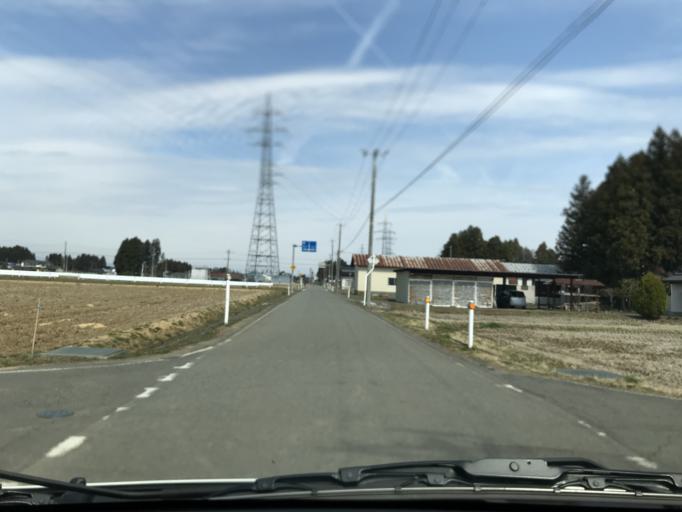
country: JP
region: Iwate
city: Mizusawa
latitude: 39.1215
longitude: 141.0857
